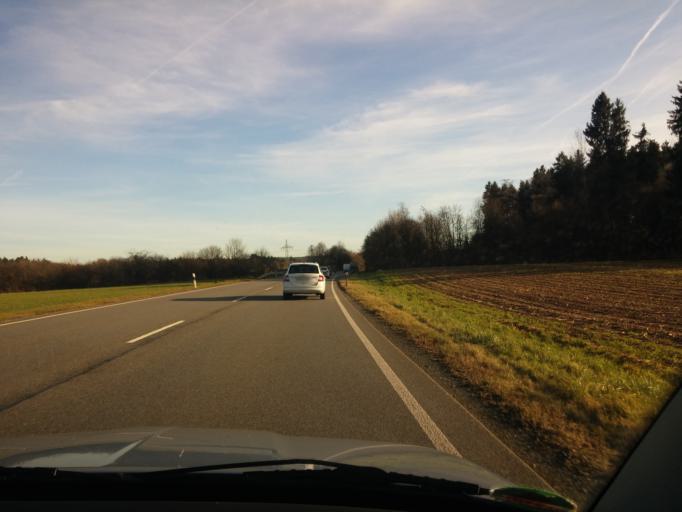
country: DE
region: Bavaria
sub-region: Upper Bavaria
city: Babensham
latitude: 48.0639
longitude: 12.2542
